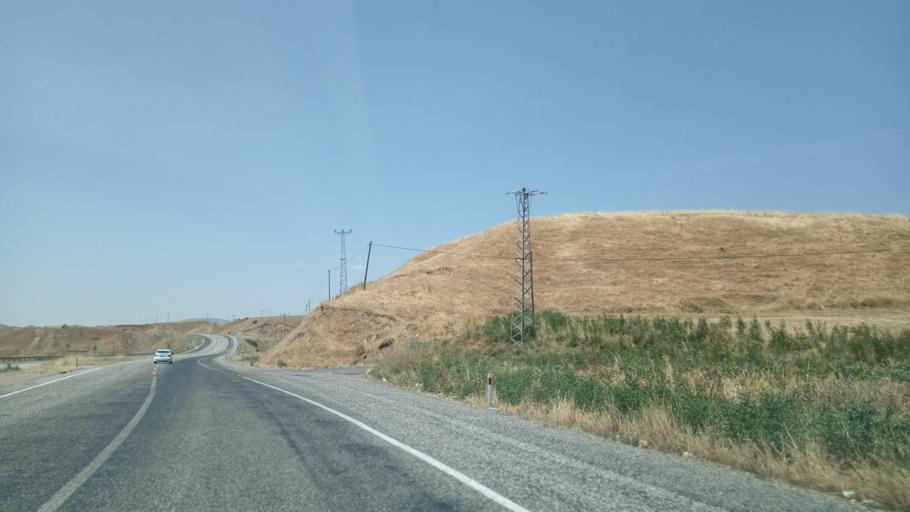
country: TR
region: Batman
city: Bekirhan
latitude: 38.1508
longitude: 41.3125
